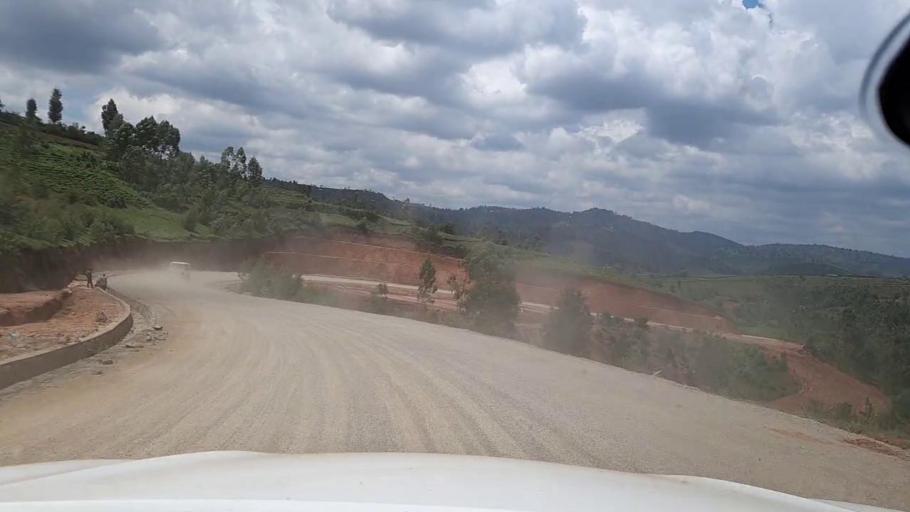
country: RW
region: Southern Province
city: Butare
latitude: -2.6935
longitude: 29.5582
